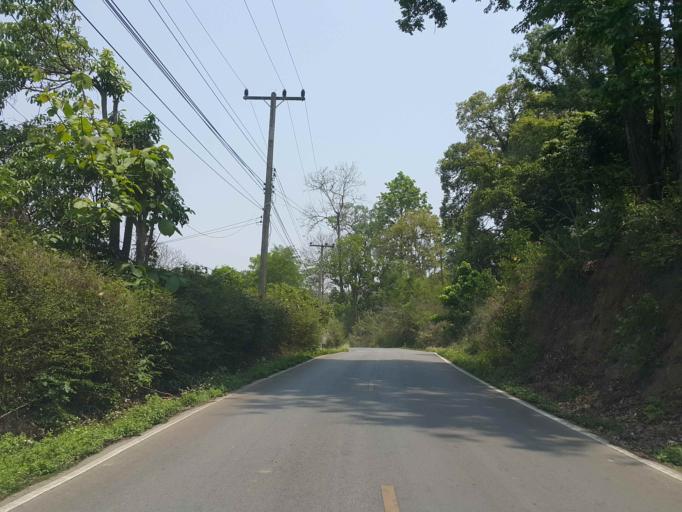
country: TH
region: Chiang Mai
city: Mae Taeng
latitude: 19.1154
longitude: 98.8946
